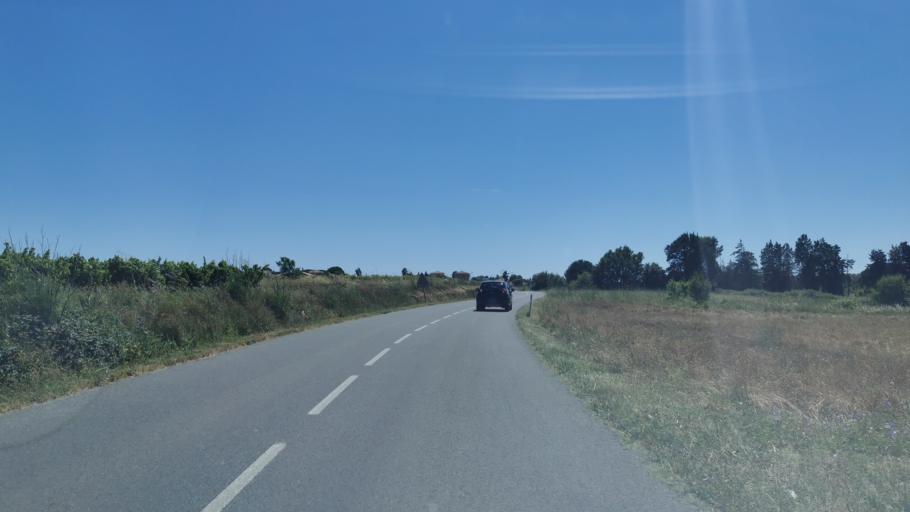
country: FR
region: Languedoc-Roussillon
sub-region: Departement de l'Aude
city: Vinassan
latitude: 43.2124
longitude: 3.0774
